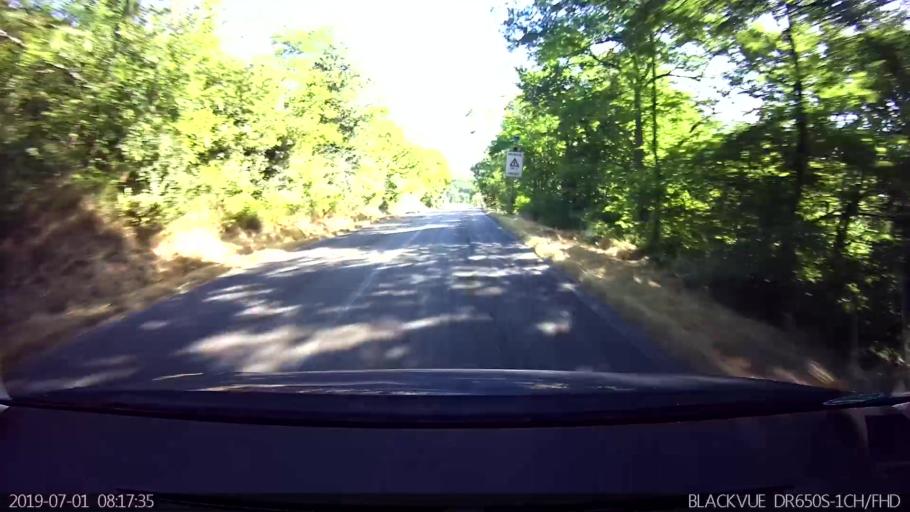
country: IT
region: Latium
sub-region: Provincia di Frosinone
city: Veroli
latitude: 41.7071
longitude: 13.4394
